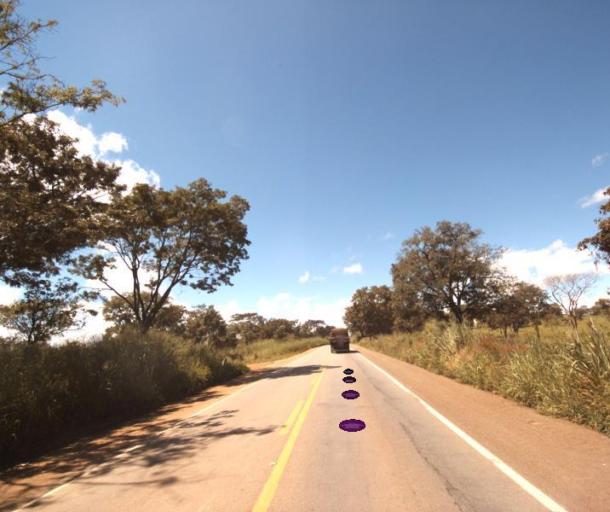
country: BR
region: Goias
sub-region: Pirenopolis
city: Pirenopolis
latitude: -16.0814
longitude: -49.0450
